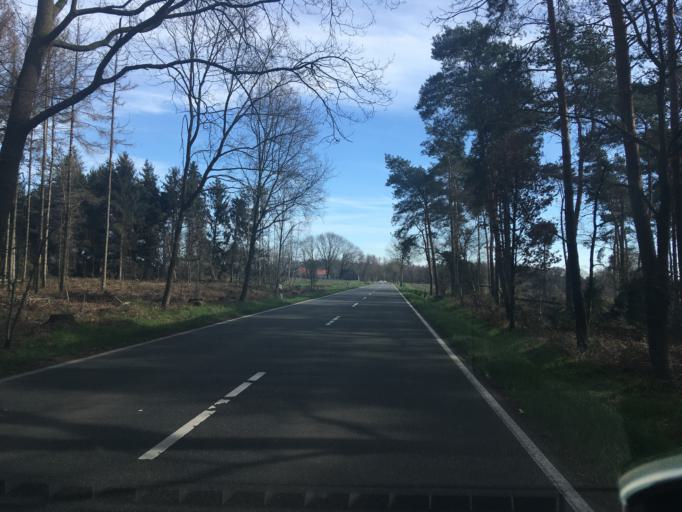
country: DE
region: North Rhine-Westphalia
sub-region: Regierungsbezirk Munster
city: Isselburg
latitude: 51.8445
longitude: 6.4821
